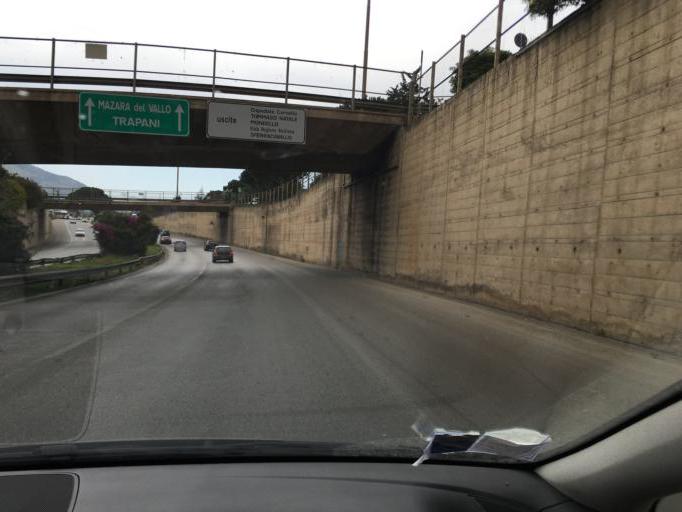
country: IT
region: Sicily
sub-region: Palermo
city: Palermo
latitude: 38.1482
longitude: 13.3269
